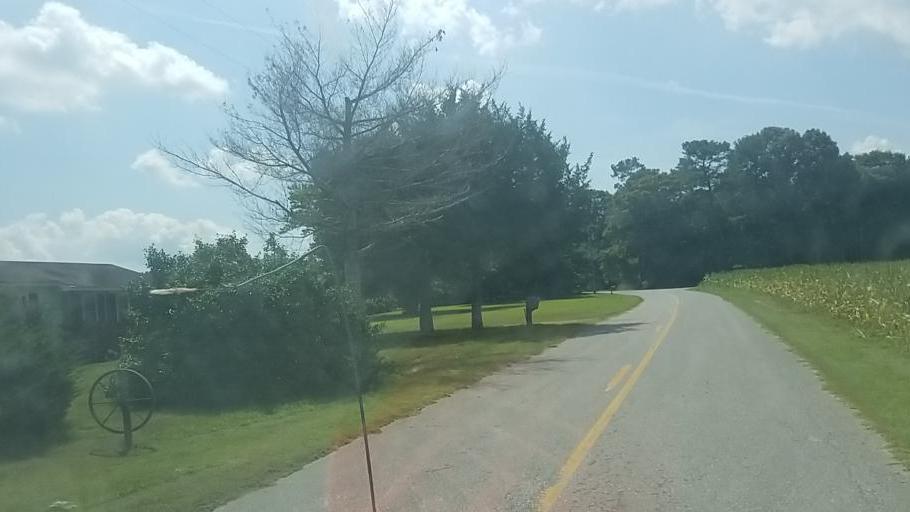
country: US
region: Maryland
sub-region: Worcester County
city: Snow Hill
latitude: 38.2508
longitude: -75.3865
